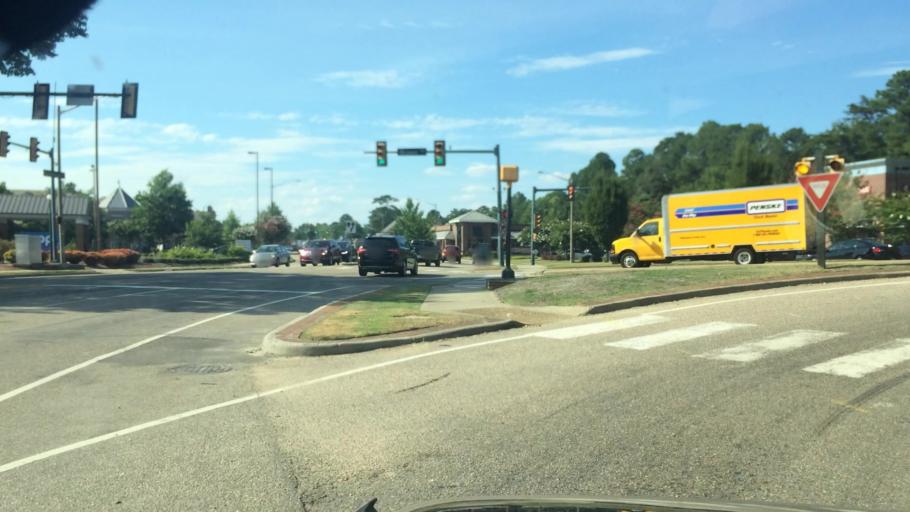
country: US
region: Virginia
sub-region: City of Williamsburg
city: Williamsburg
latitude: 37.2867
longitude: -76.7215
